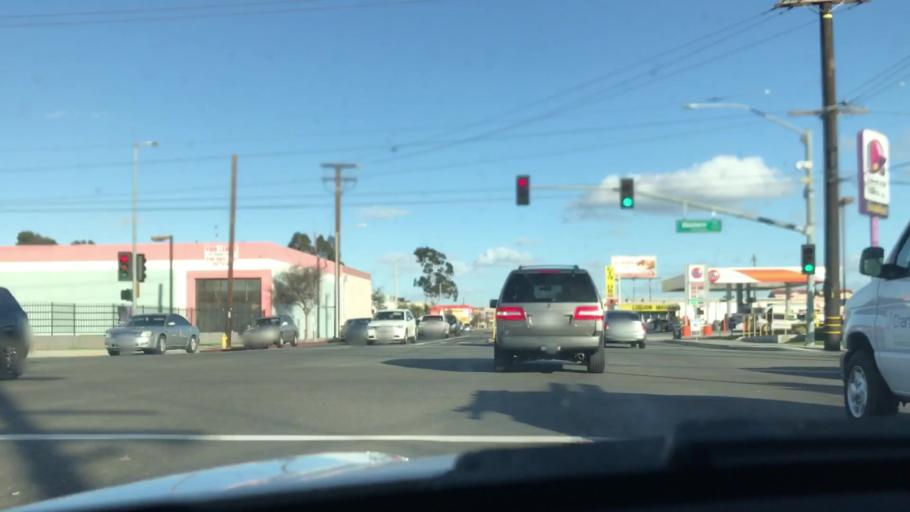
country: US
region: California
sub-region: Los Angeles County
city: Gardena
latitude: 33.9019
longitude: -118.3094
